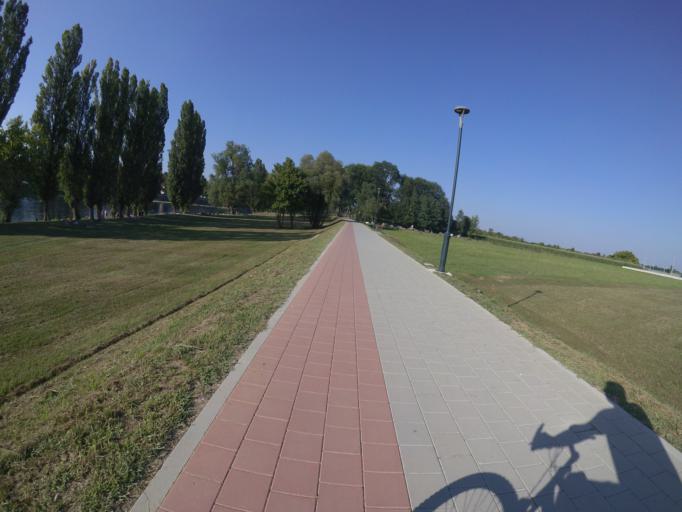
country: HR
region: Karlovacka
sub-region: Grad Karlovac
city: Karlovac
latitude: 45.4860
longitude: 15.5622
